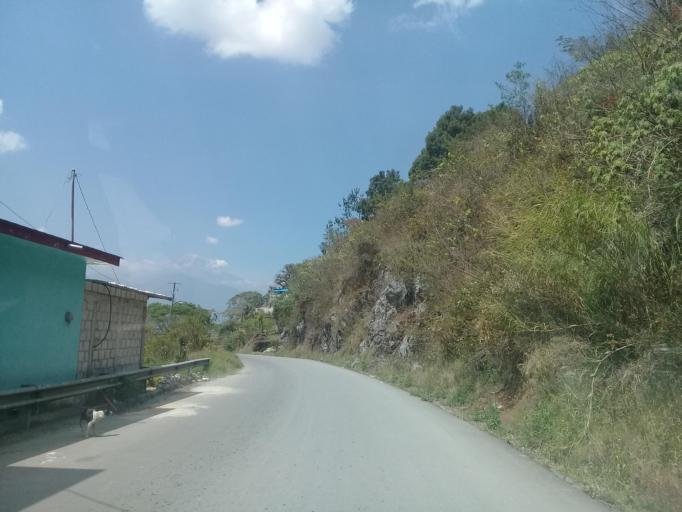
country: MX
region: Veracruz
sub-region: Tlilapan
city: Tonalixco
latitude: 18.7978
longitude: -97.0559
